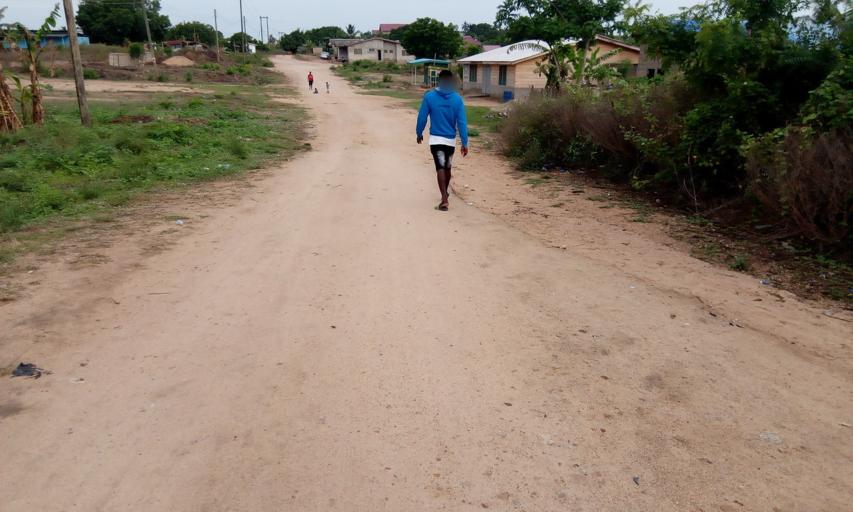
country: GH
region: Central
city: Winneba
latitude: 5.3573
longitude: -0.6193
